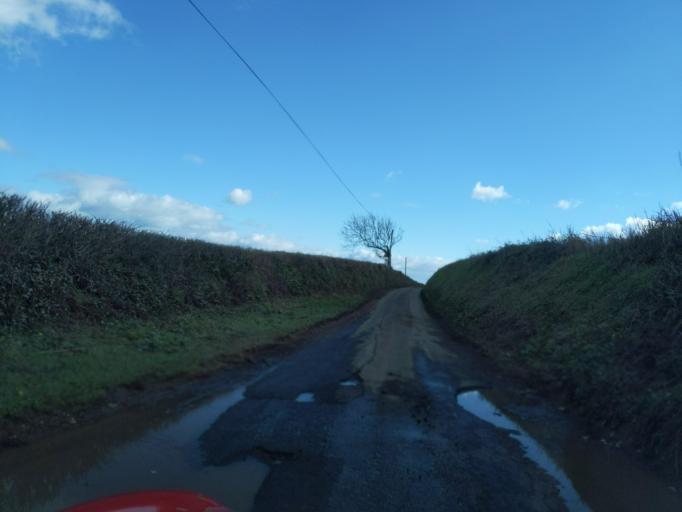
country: GB
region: England
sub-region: Devon
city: Kingsbridge
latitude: 50.2981
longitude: -3.7912
